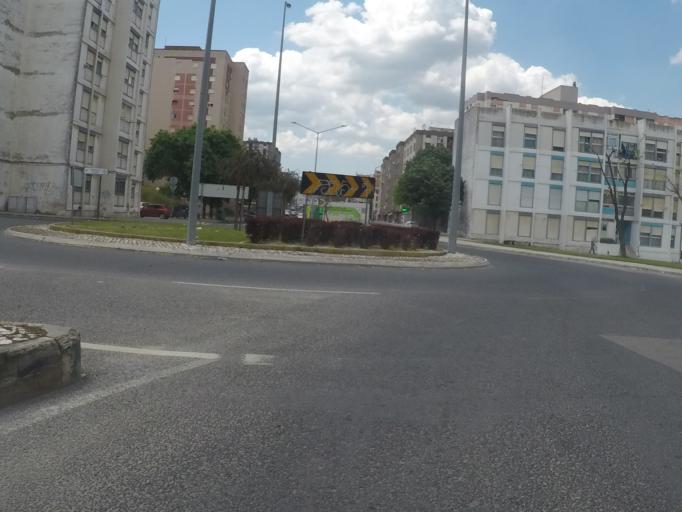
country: PT
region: Setubal
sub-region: Setubal
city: Setubal
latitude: 38.5259
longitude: -8.8687
